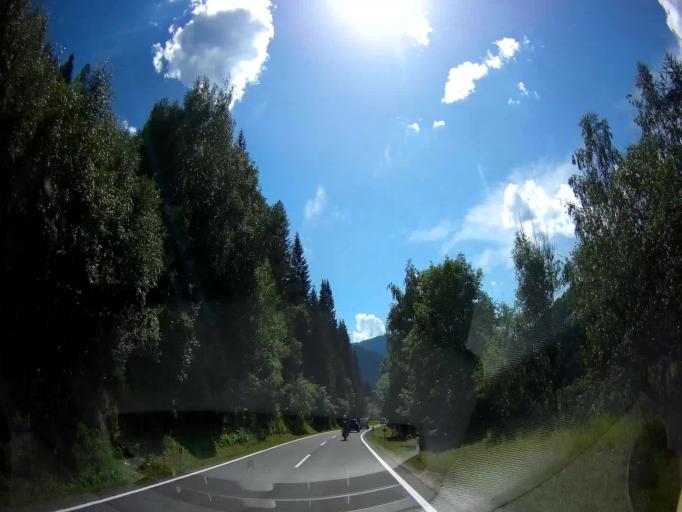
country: AT
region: Styria
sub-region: Politischer Bezirk Murau
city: Stadl an der Mur
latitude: 47.0744
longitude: 13.9202
